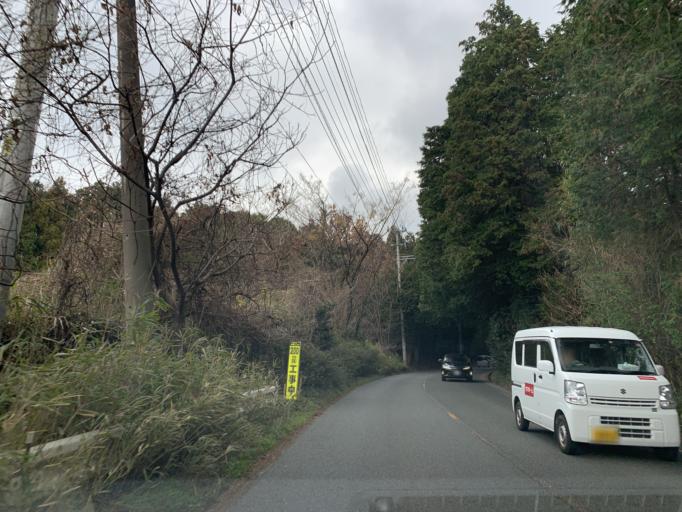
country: JP
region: Kumamoto
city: Ozu
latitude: 32.8852
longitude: 130.8941
